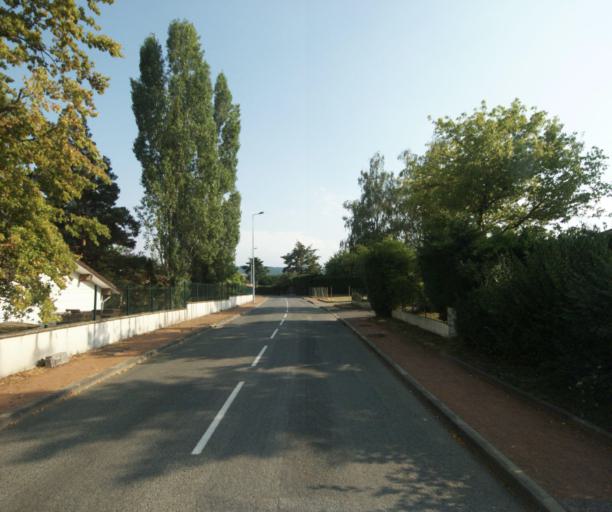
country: FR
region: Rhone-Alpes
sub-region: Departement du Rhone
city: Sain-Bel
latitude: 45.8151
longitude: 4.5979
